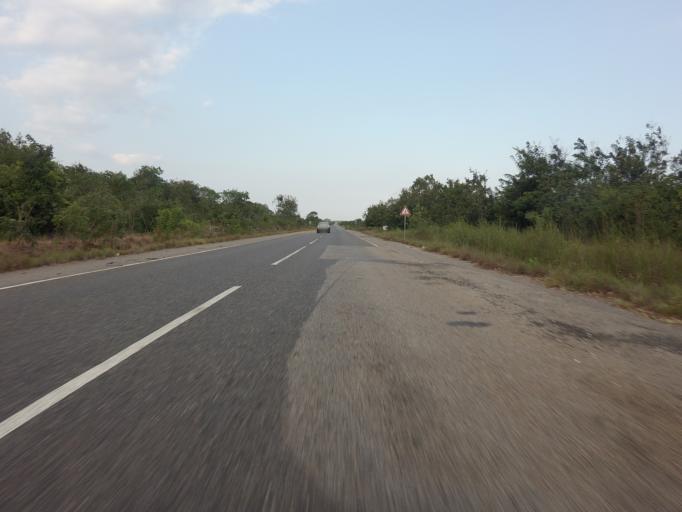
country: GH
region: Volta
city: Anloga
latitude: 6.0849
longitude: 0.5555
